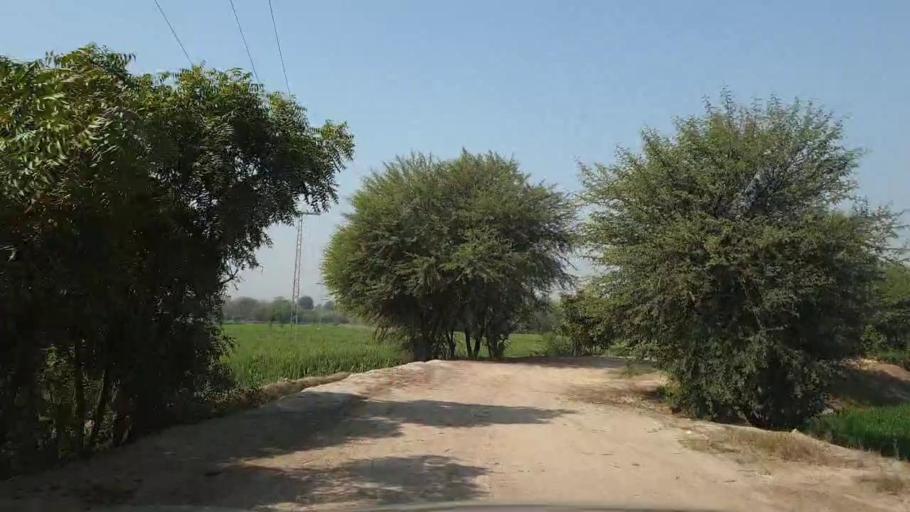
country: PK
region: Sindh
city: Tando Allahyar
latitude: 25.4678
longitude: 68.6983
